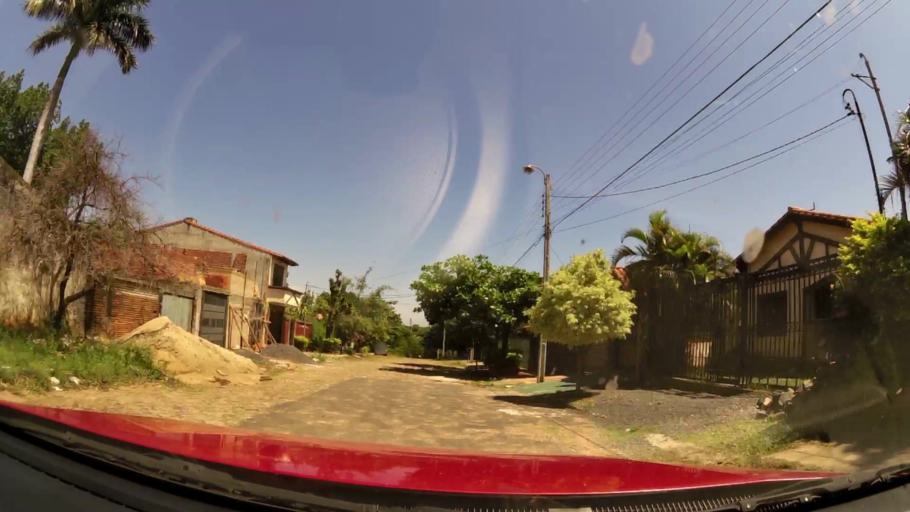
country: PY
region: Central
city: Colonia Mariano Roque Alonso
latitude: -25.2360
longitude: -57.5515
